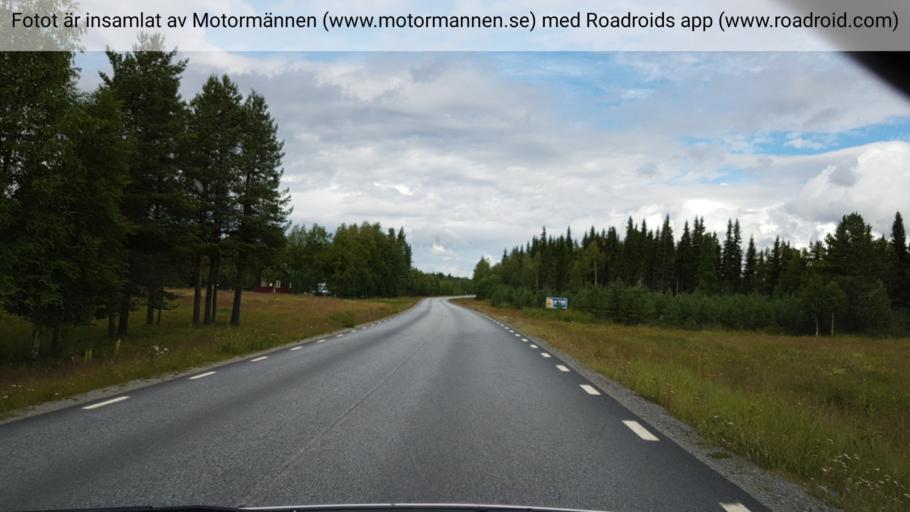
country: SE
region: Vaesterbotten
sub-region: Vilhelmina Kommun
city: Vilhelmina
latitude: 64.4562
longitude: 16.8138
